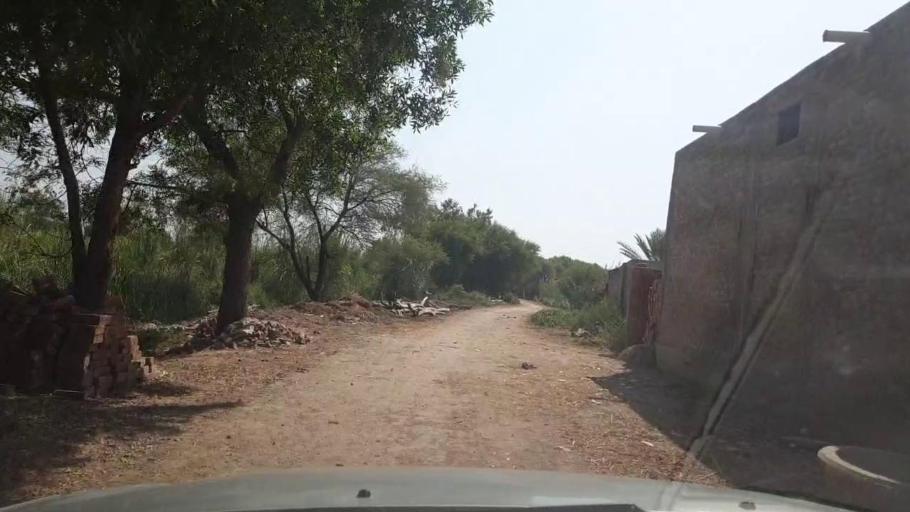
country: PK
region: Sindh
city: Bulri
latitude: 24.8818
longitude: 68.4034
